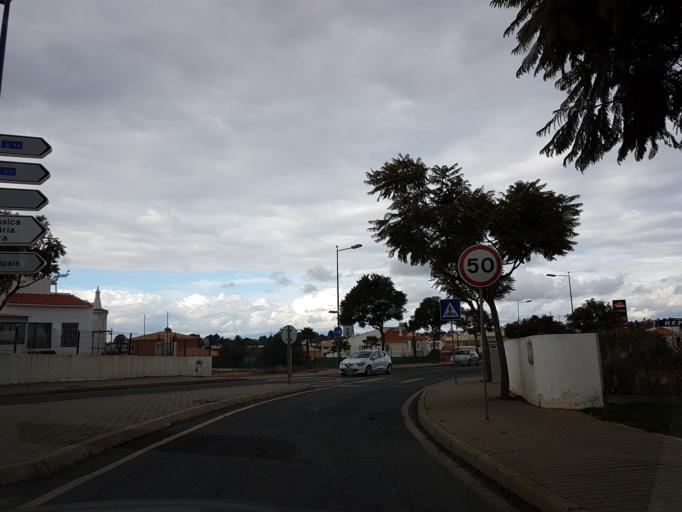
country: PT
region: Faro
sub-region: Albufeira
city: Ferreiras
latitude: 37.1051
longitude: -8.2300
